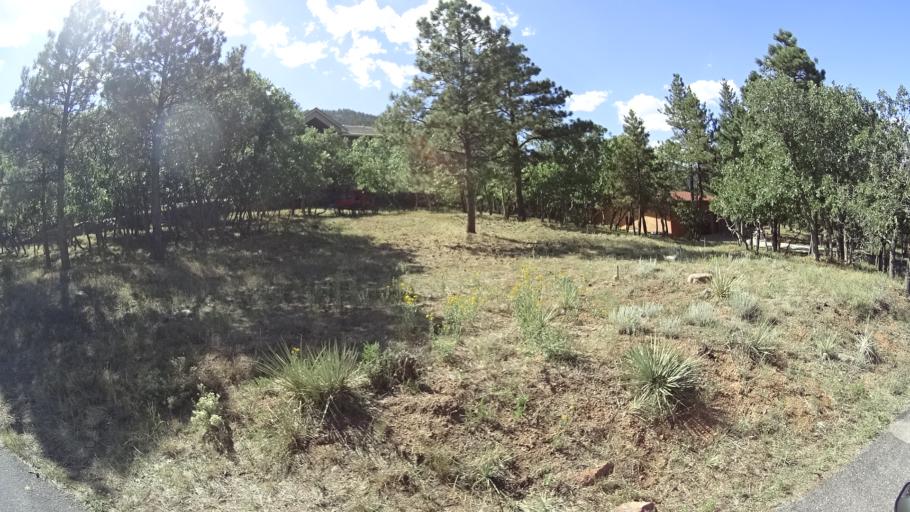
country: US
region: Colorado
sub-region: El Paso County
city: Manitou Springs
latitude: 38.8120
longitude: -104.8788
